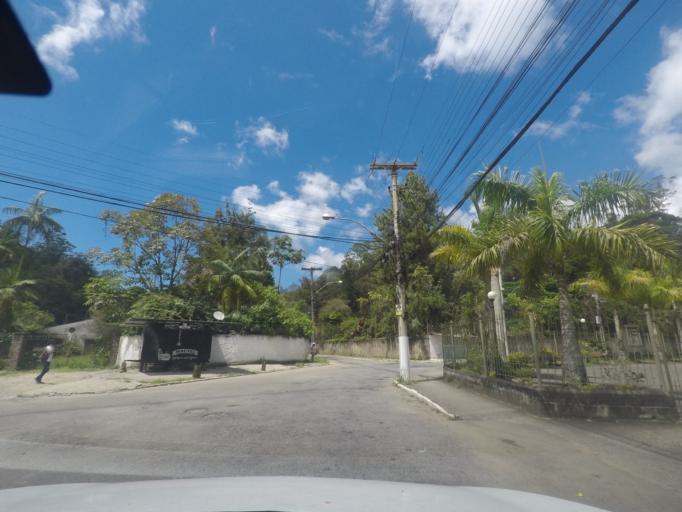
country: BR
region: Rio de Janeiro
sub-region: Teresopolis
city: Teresopolis
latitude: -22.4113
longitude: -42.9810
